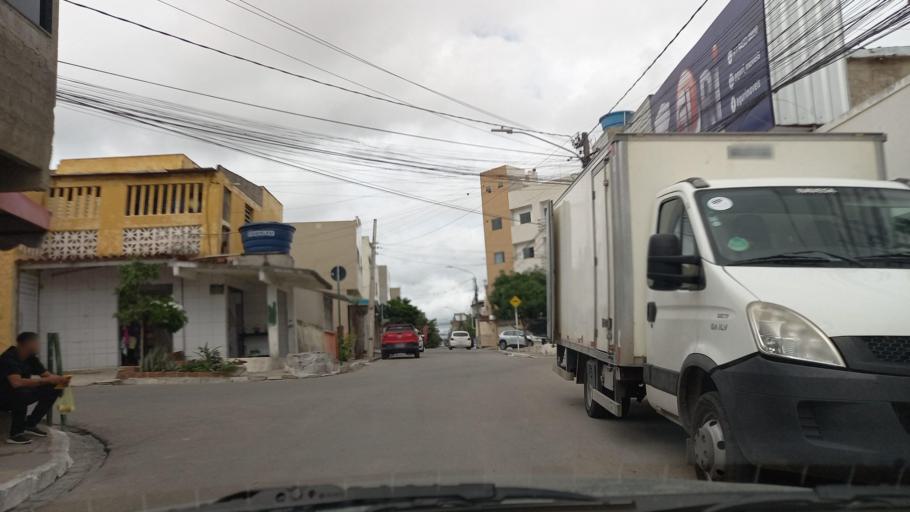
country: BR
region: Pernambuco
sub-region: Caruaru
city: Caruaru
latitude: -8.2708
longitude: -35.9595
